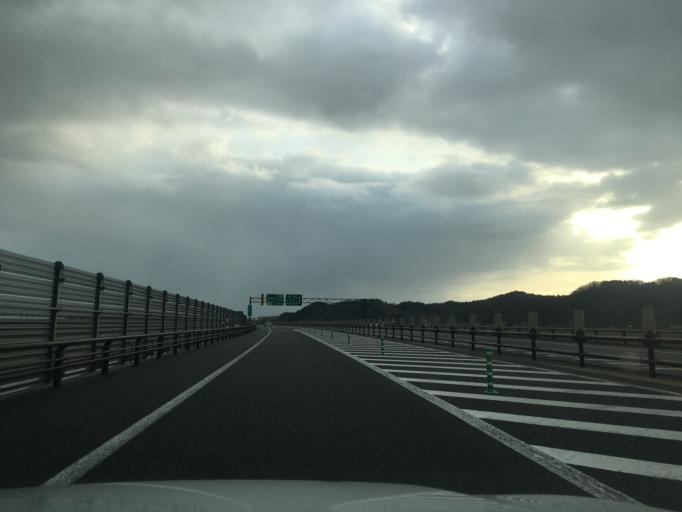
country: JP
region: Yamagata
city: Tsuruoka
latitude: 38.7118
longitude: 139.7495
